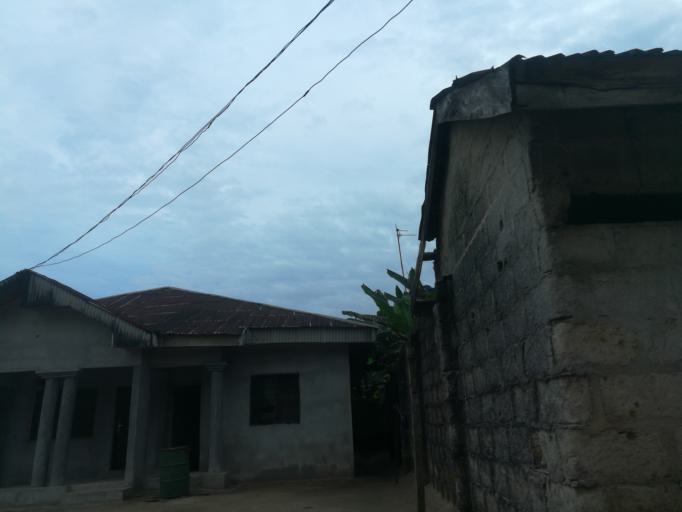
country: NG
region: Rivers
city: Port Harcourt
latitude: 4.7934
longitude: 6.9590
